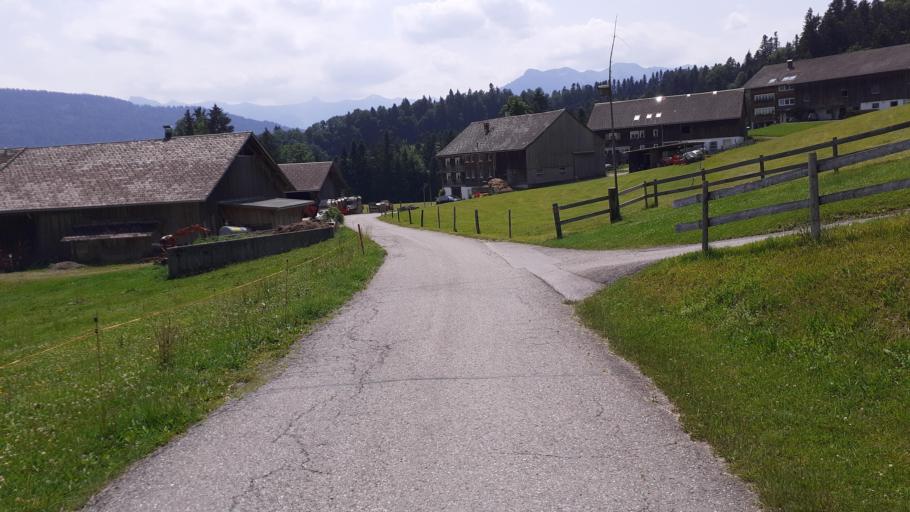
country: AT
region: Vorarlberg
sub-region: Politischer Bezirk Bregenz
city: Egg
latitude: 47.4378
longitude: 9.8840
